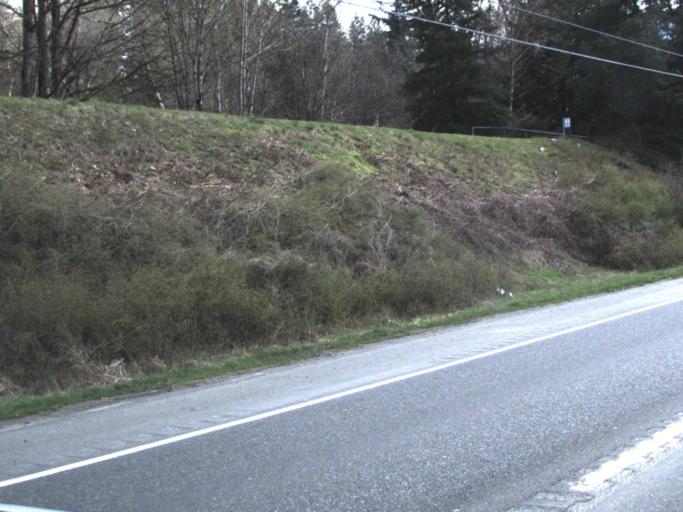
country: US
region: Washington
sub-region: King County
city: Maple Valley
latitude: 47.4115
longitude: -122.0404
